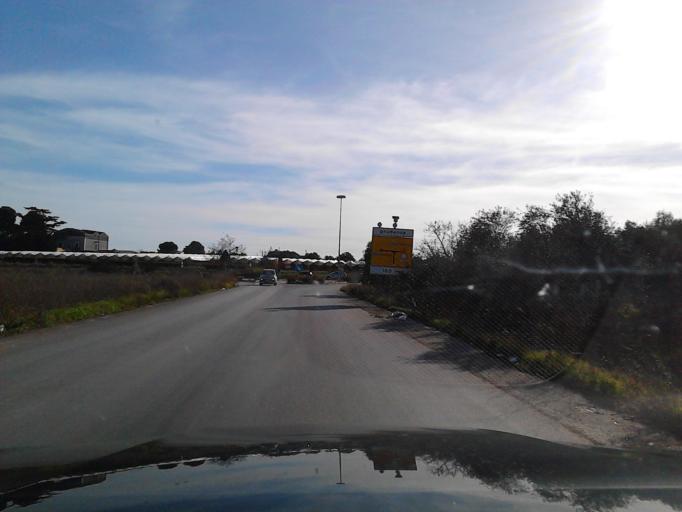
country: IT
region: Apulia
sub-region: Provincia di Bari
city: Rutigliano
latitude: 41.0085
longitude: 16.9890
